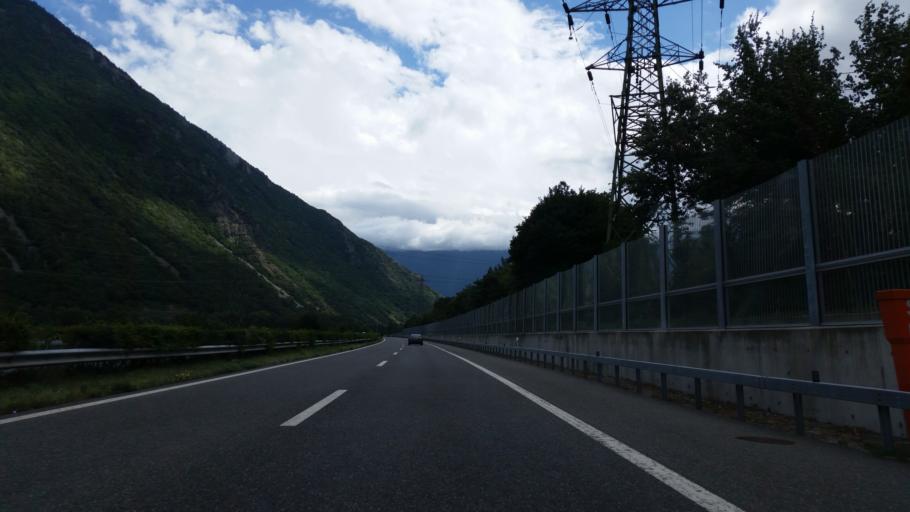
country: CH
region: Valais
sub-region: Saint-Maurice District
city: Vernayaz
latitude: 46.1396
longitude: 7.0420
